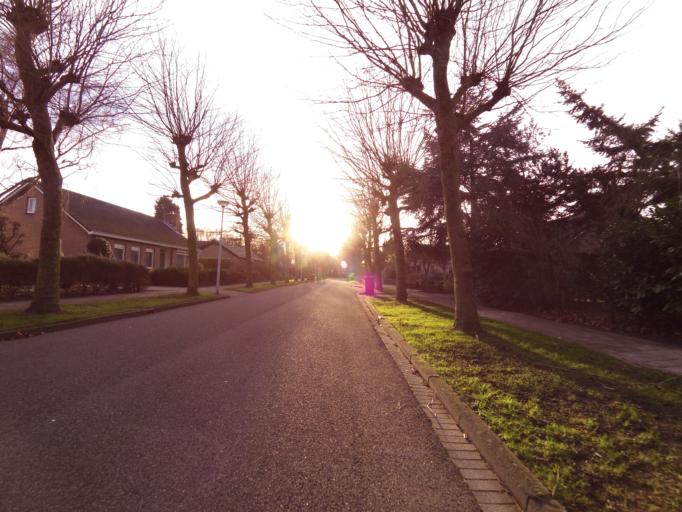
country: NL
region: South Holland
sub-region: Gemeente Brielle
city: Brielle
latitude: 51.9108
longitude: 4.0941
